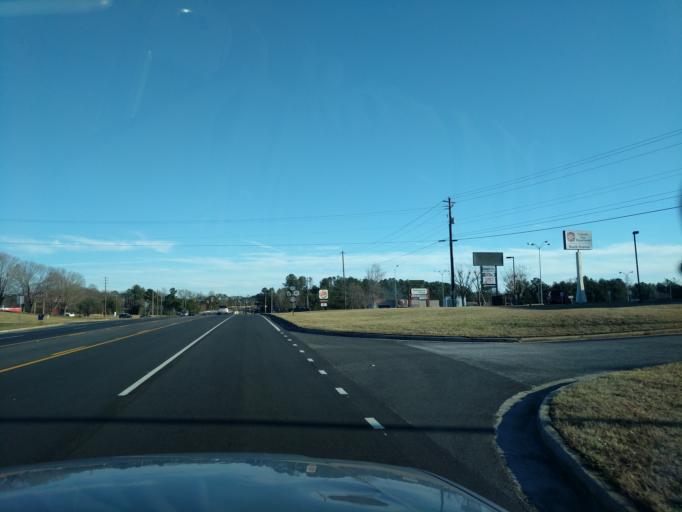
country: US
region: Georgia
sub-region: Habersham County
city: Demorest
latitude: 34.5424
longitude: -83.5431
